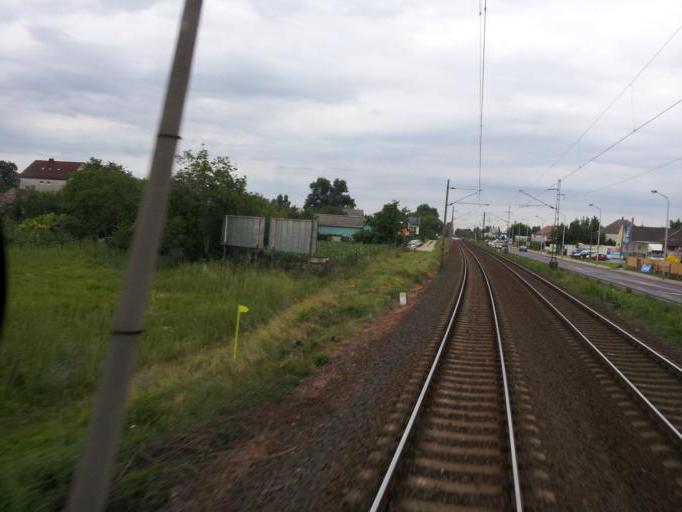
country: HU
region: Fejer
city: Szekesfehervar
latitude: 47.1714
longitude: 18.4056
